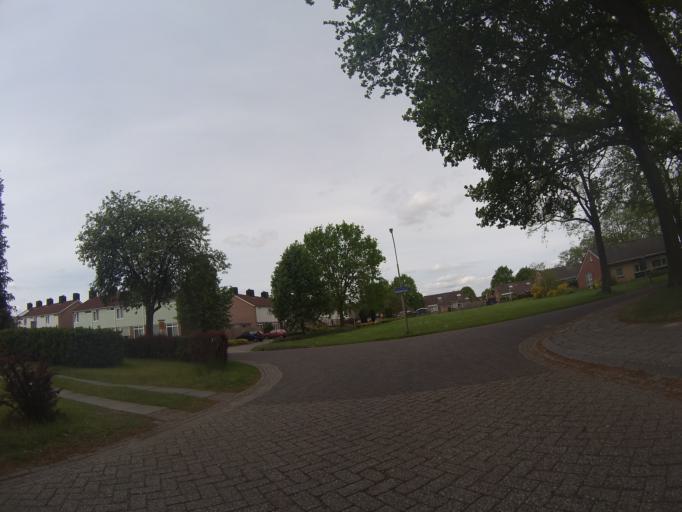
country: NL
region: Drenthe
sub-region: Gemeente Borger-Odoorn
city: Borger
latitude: 52.8459
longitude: 6.7539
